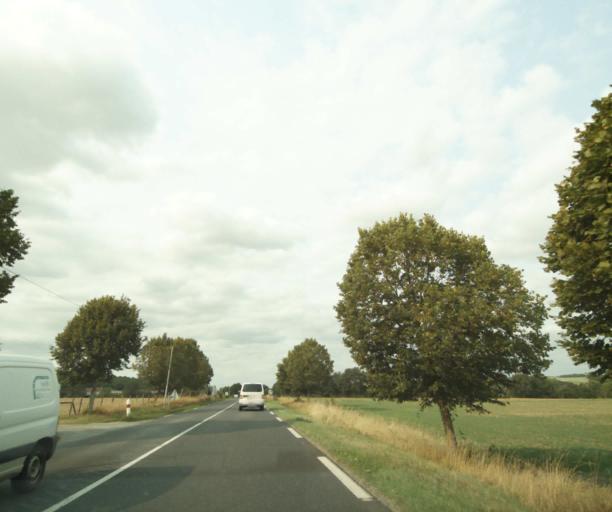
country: FR
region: Centre
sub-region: Departement de l'Indre
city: Chatillon-sur-Indre
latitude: 47.0344
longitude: 1.0956
